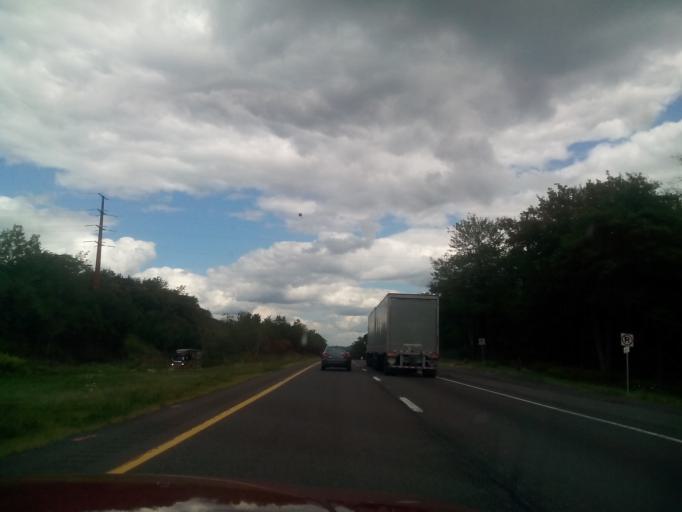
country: US
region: Pennsylvania
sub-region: Carbon County
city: Towamensing Trails
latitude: 41.0824
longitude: -75.6358
